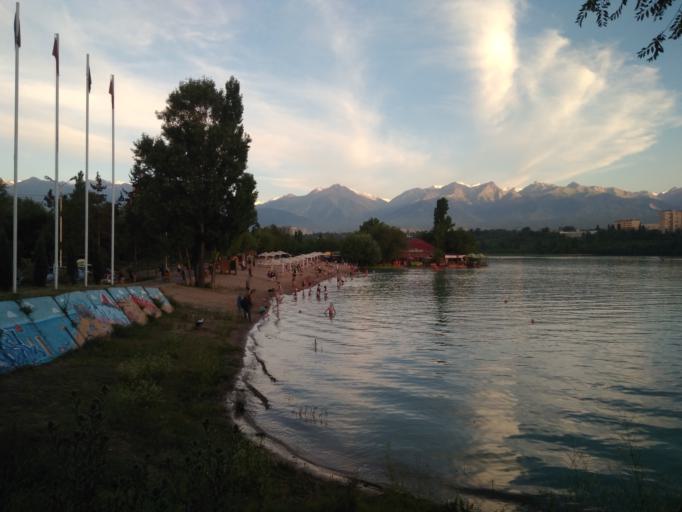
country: KZ
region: Almaty Qalasy
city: Almaty
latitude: 43.2477
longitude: 76.8664
